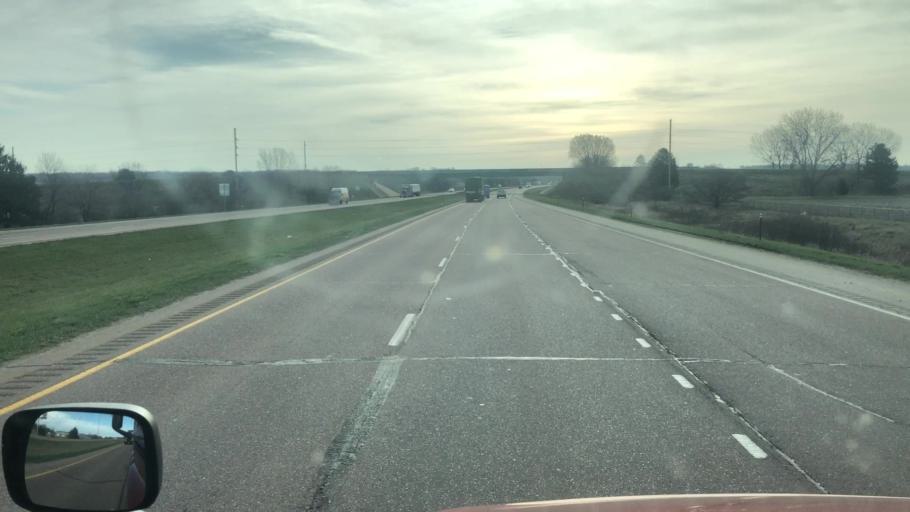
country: US
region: Nebraska
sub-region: Dakota County
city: South Sioux City
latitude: 42.4493
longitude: -96.4073
